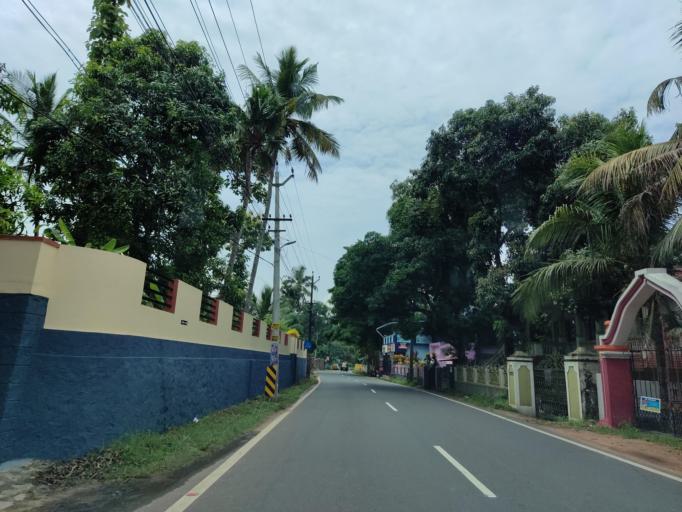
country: IN
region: Kerala
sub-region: Alappuzha
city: Chengannur
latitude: 9.2975
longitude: 76.6263
